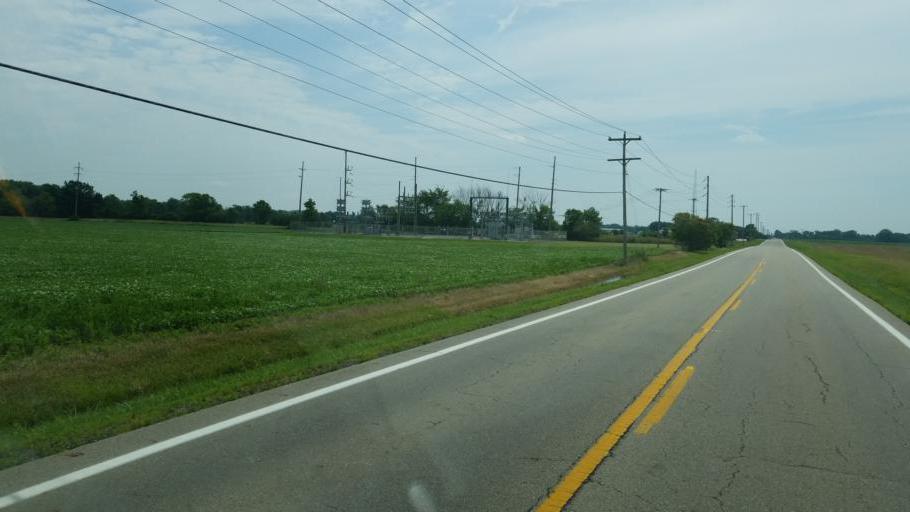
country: US
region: Ohio
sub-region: Madison County
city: West Jefferson
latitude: 39.9705
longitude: -83.3701
